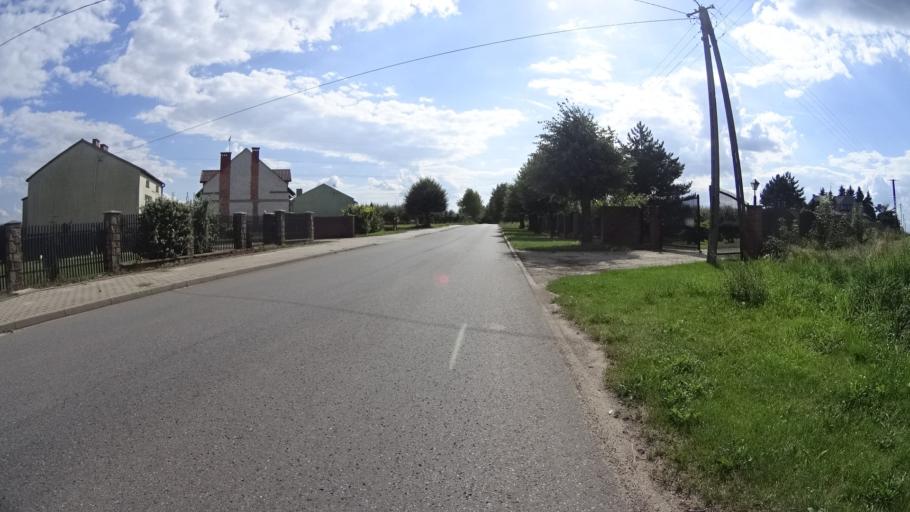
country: PL
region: Masovian Voivodeship
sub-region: Powiat grojecki
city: Mogielnica
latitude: 51.6840
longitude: 20.7164
